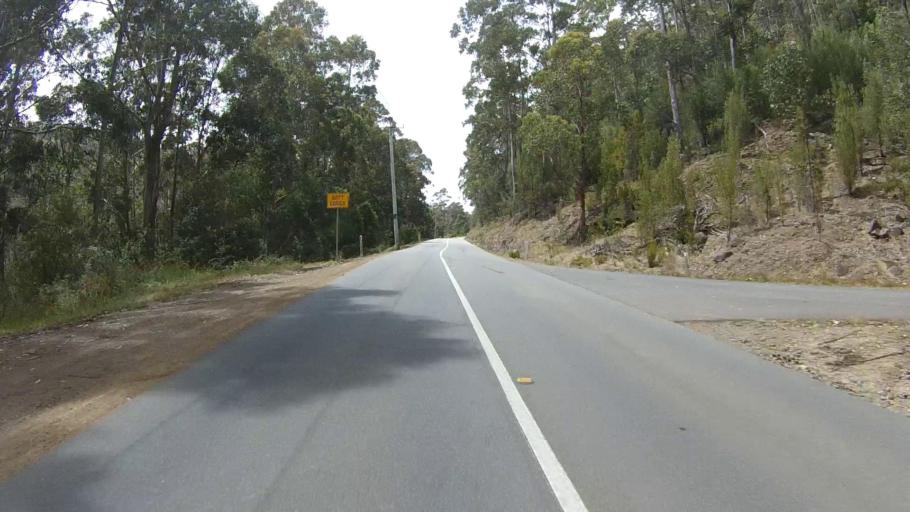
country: AU
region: Tasmania
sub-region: Kingborough
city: Kettering
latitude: -43.1264
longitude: 147.1714
